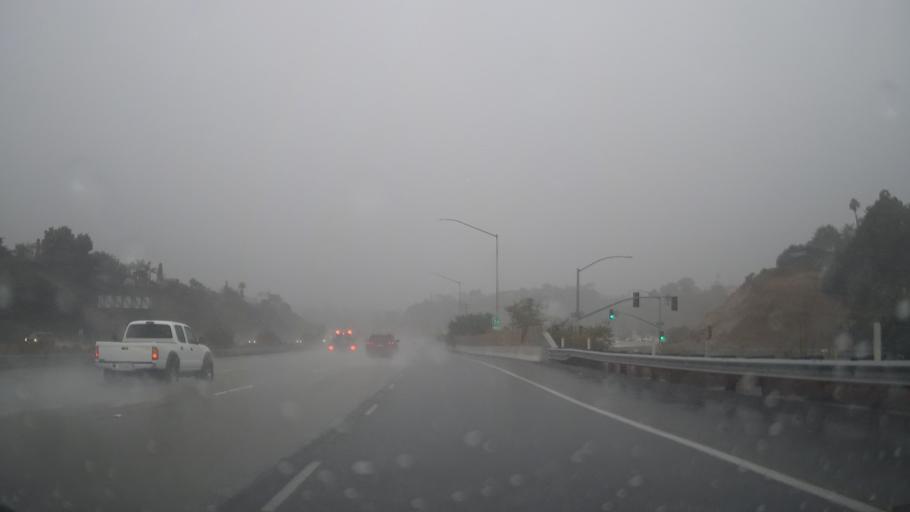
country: US
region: California
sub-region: San Diego County
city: Bonita
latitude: 32.6640
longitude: -117.0605
